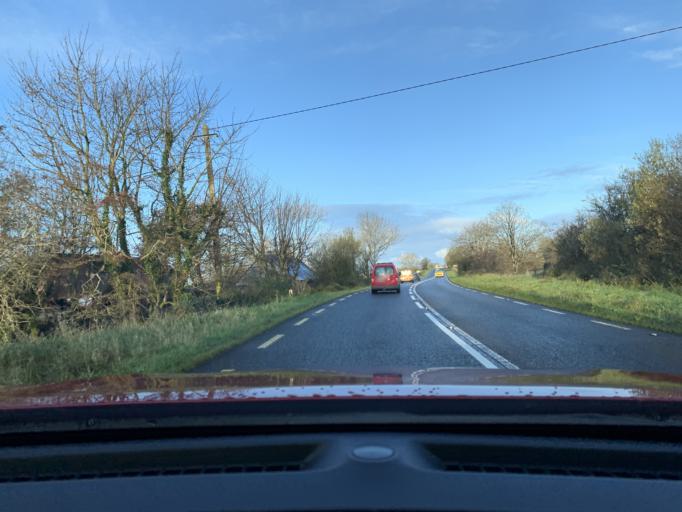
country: IE
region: Connaught
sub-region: Sligo
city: Sligo
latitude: 54.3544
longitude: -8.5136
